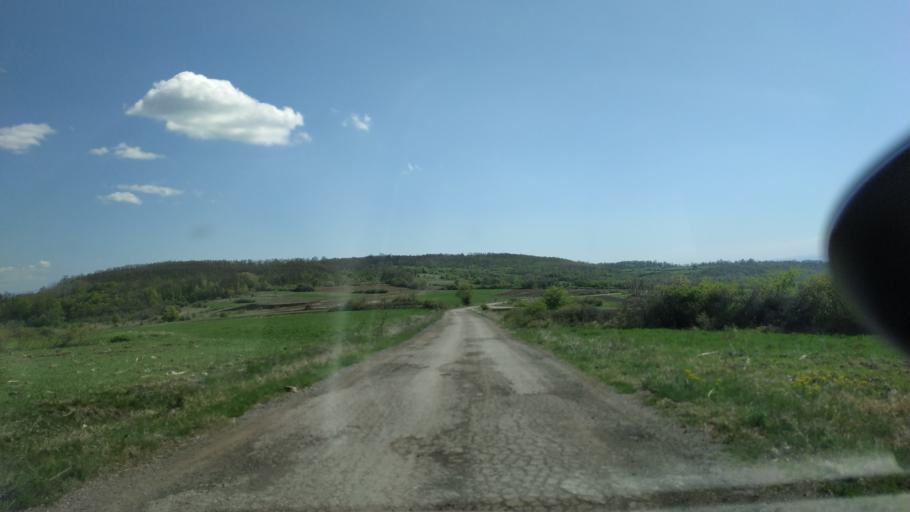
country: RS
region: Central Serbia
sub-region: Zajecarski Okrug
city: Soko Banja
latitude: 43.5169
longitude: 21.9056
